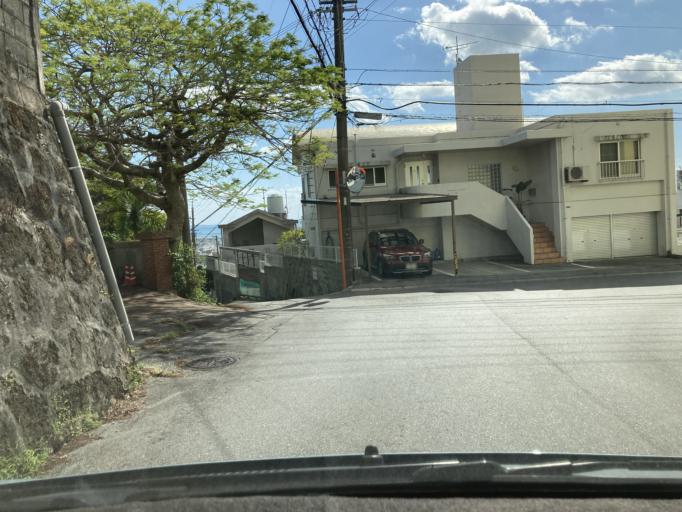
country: JP
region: Okinawa
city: Okinawa
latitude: 26.3275
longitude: 127.8170
